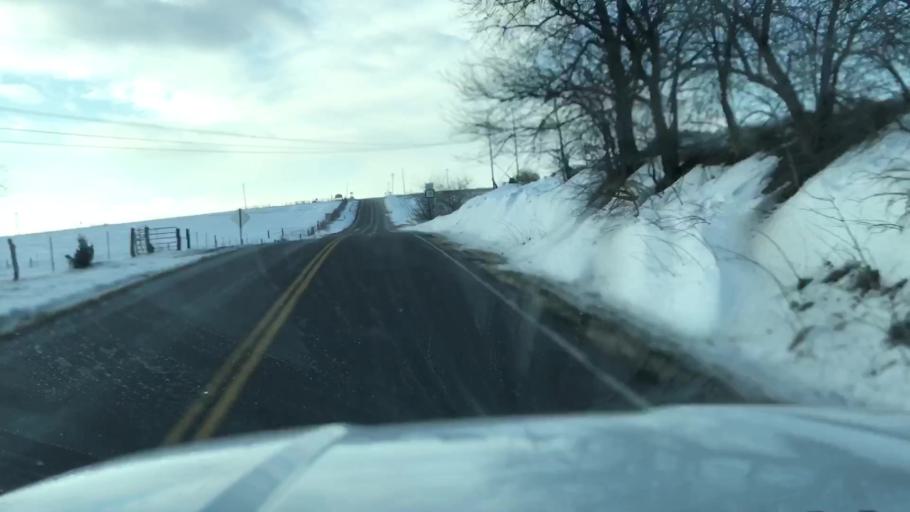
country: US
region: Missouri
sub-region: Nodaway County
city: Maryville
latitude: 40.2019
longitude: -94.9496
